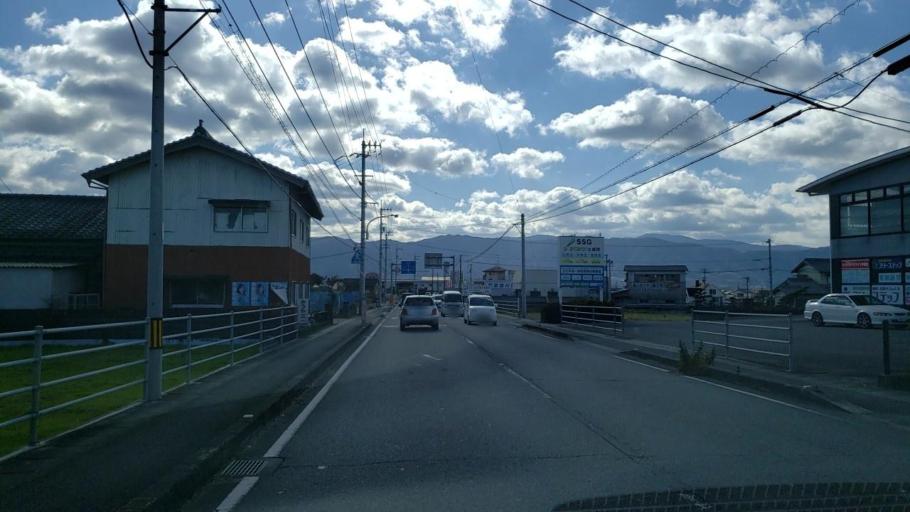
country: JP
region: Tokushima
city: Kamojimacho-jogejima
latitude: 34.1003
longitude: 134.3451
